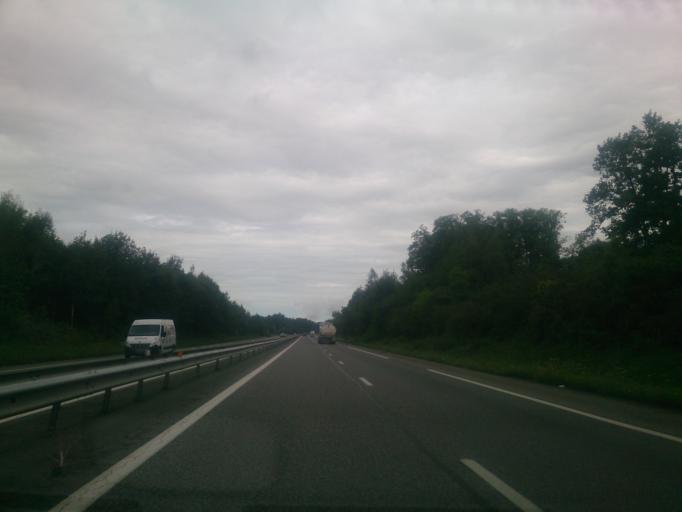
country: FR
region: Midi-Pyrenees
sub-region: Departement de la Haute-Garonne
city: Montrejeau
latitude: 43.1020
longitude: 0.4811
